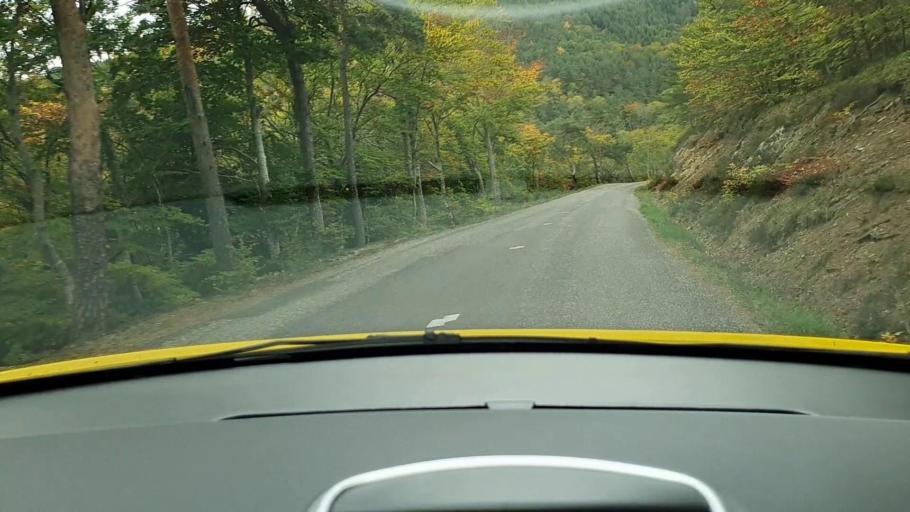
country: FR
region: Languedoc-Roussillon
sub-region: Departement de la Lozere
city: Meyrueis
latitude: 44.0759
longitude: 3.4110
